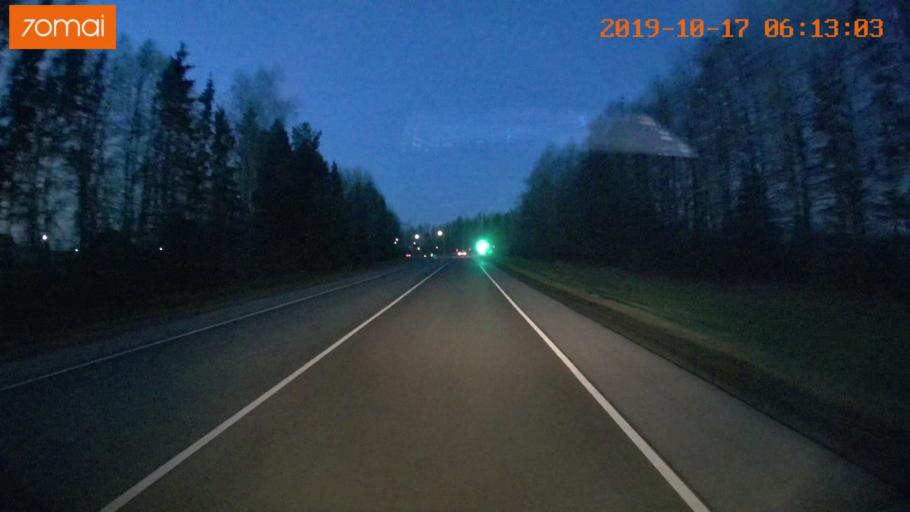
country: RU
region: Ivanovo
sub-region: Gorod Ivanovo
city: Ivanovo
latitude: 56.9035
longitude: 40.9397
